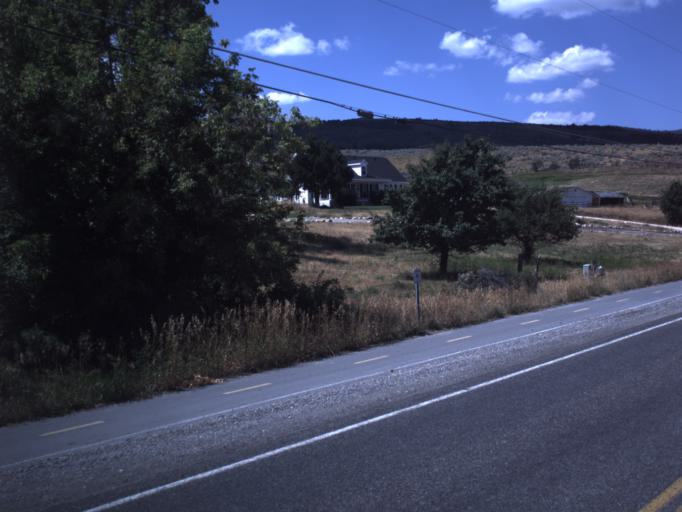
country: US
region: Idaho
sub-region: Bear Lake County
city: Paris
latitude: 41.9212
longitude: -111.3947
